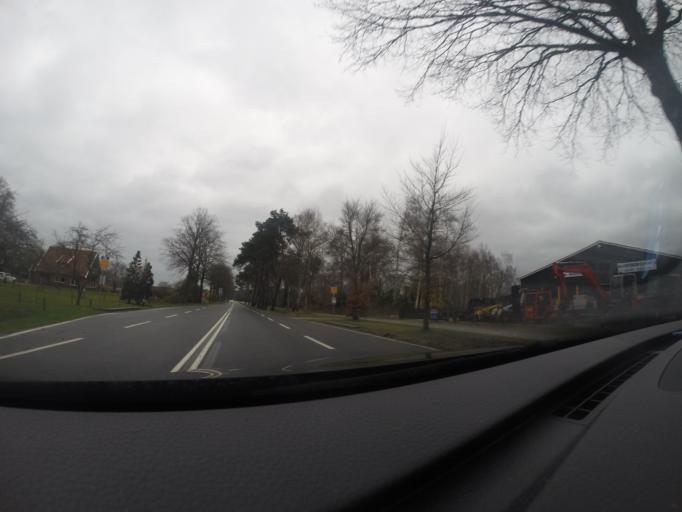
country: NL
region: Overijssel
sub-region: Gemeente Hof van Twente
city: Hengevelde
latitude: 52.2136
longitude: 6.6668
